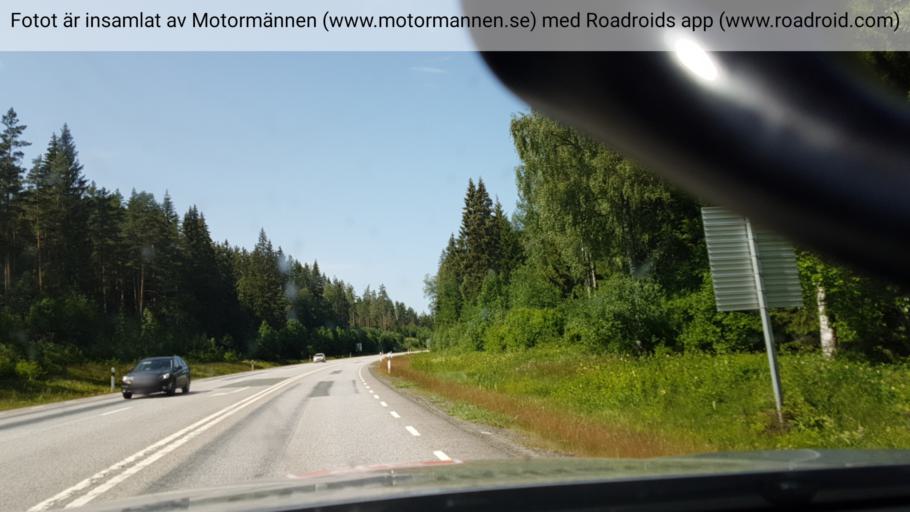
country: SE
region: Joenkoeping
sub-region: Aneby Kommun
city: Aneby
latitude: 57.7732
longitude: 14.8887
